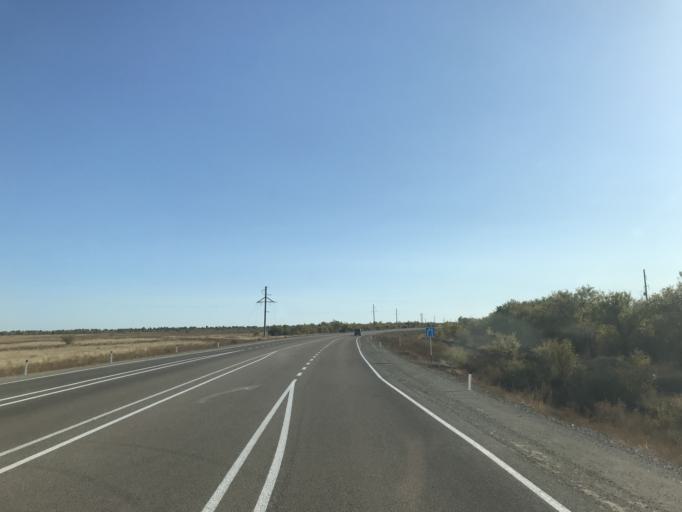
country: KZ
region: Pavlodar
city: Koktobe
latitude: 51.7276
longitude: 77.5597
